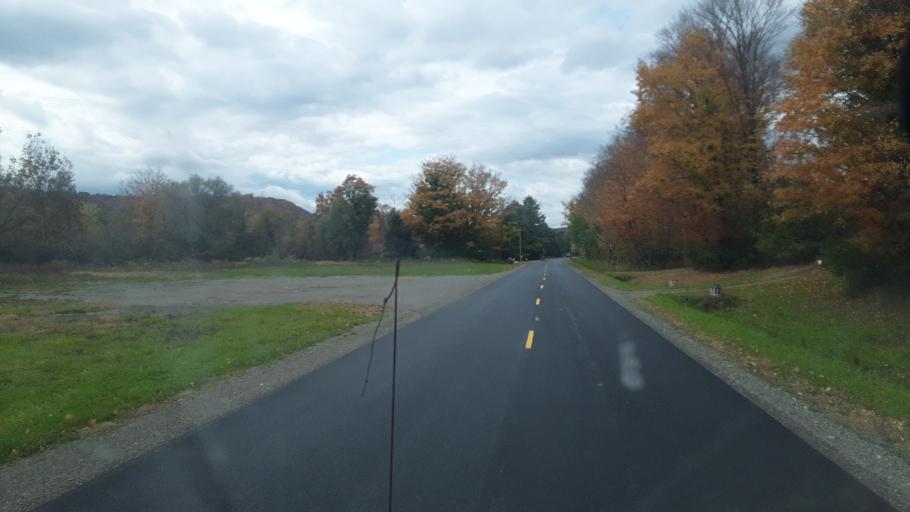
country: US
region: New York
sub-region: Allegany County
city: Alfred
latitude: 42.3666
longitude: -77.7778
